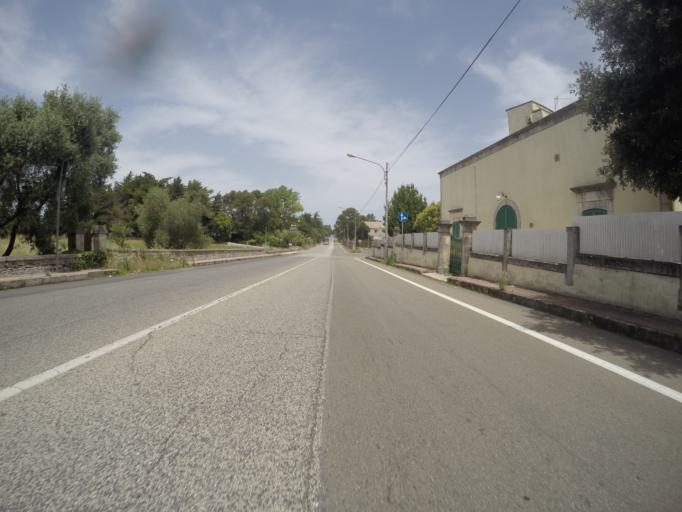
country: IT
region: Apulia
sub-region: Provincia di Taranto
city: Martina Franca
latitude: 40.6893
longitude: 17.3339
